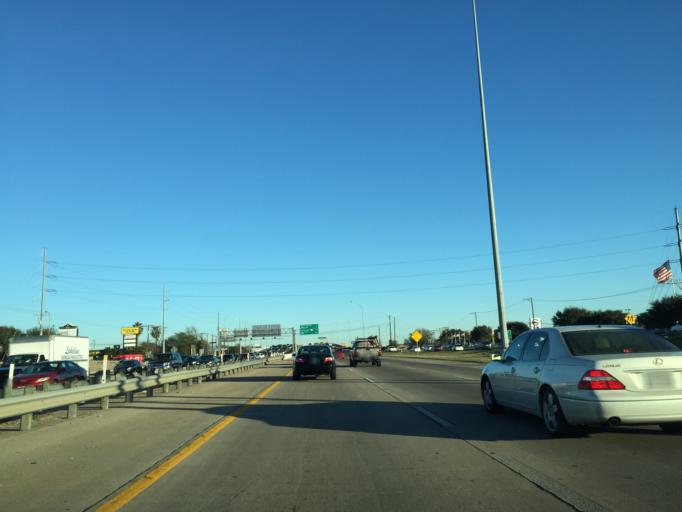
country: US
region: Texas
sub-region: Williamson County
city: Jollyville
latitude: 30.3756
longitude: -97.7316
